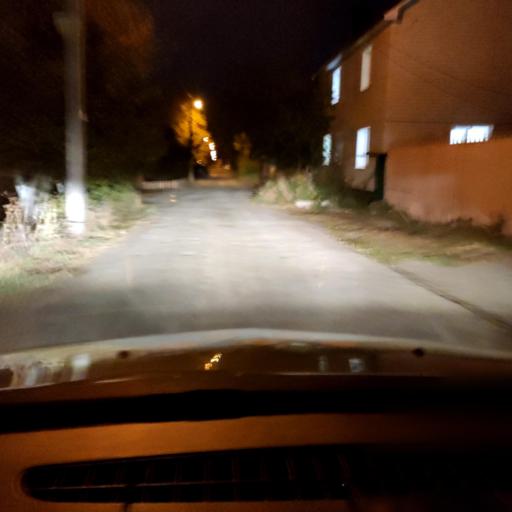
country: RU
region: Voronezj
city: Voronezh
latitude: 51.6596
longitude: 39.1641
